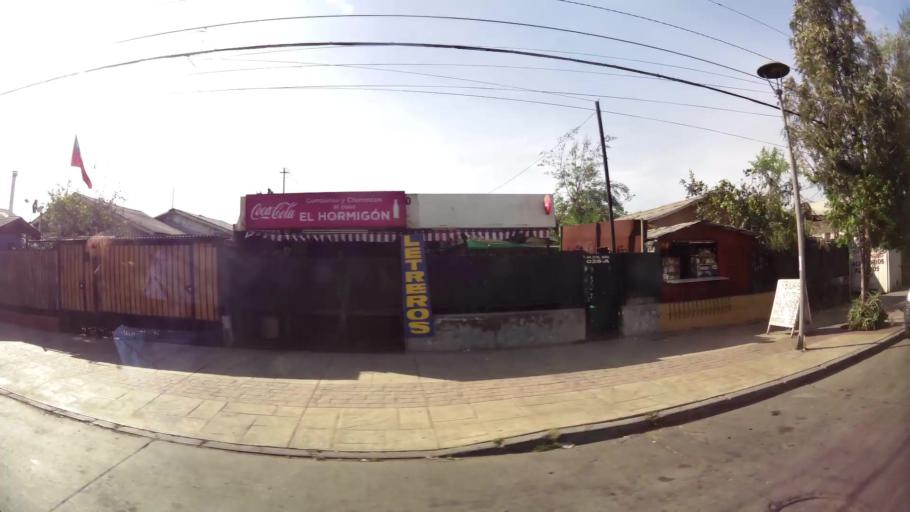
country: CL
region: Santiago Metropolitan
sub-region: Provincia de Santiago
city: La Pintana
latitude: -33.5255
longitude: -70.6351
